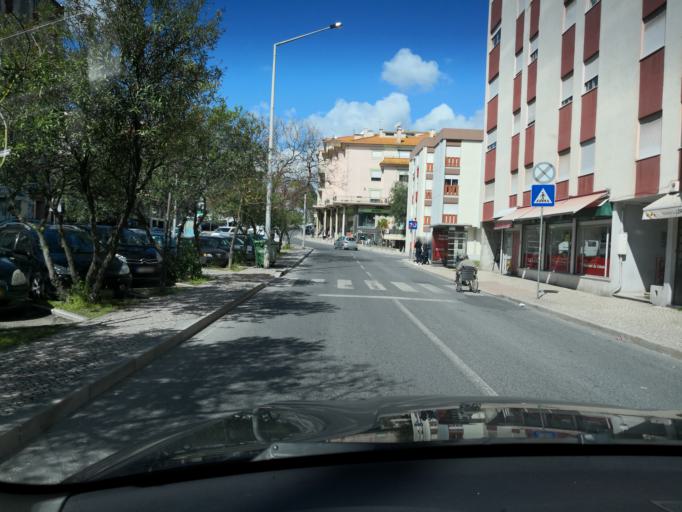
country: PT
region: Setubal
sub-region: Setubal
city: Setubal
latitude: 38.5258
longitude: -8.8709
